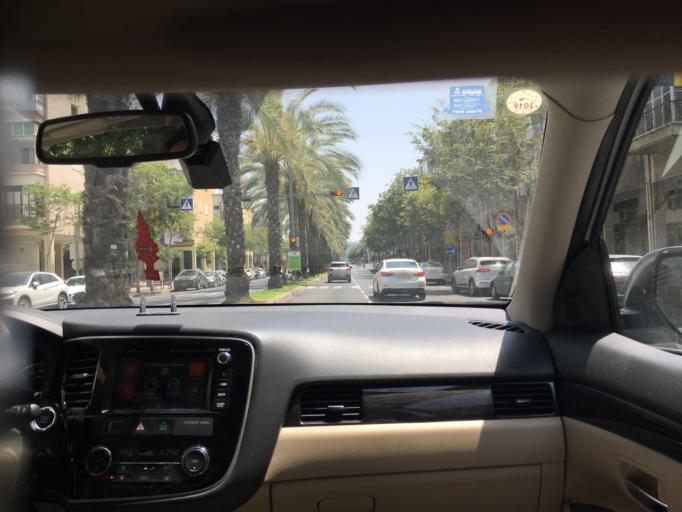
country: IL
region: Tel Aviv
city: Tel Aviv
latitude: 32.0931
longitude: 34.7832
